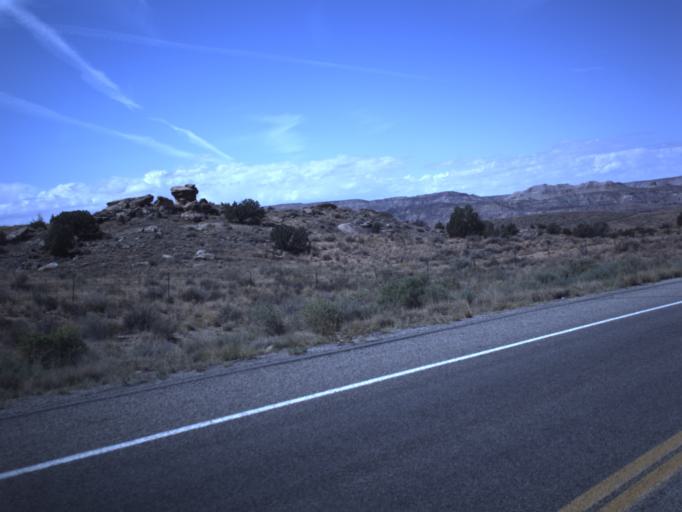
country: US
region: Colorado
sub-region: Montezuma County
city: Towaoc
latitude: 37.1913
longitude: -109.1361
